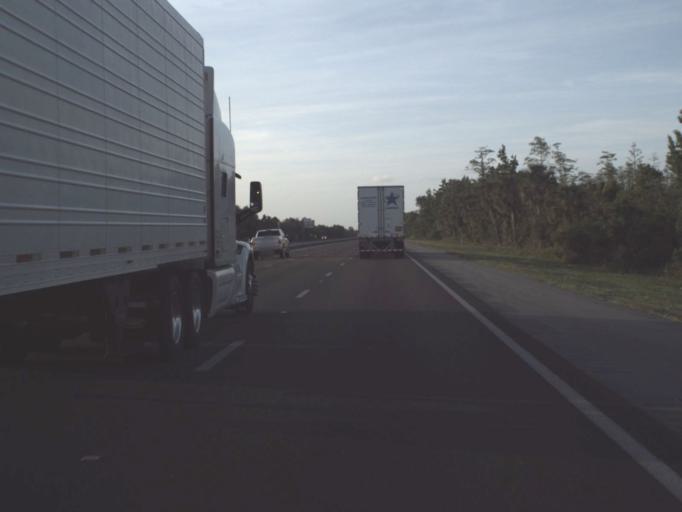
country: US
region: Florida
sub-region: Volusia County
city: Oak Hill
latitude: 28.7856
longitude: -80.8978
